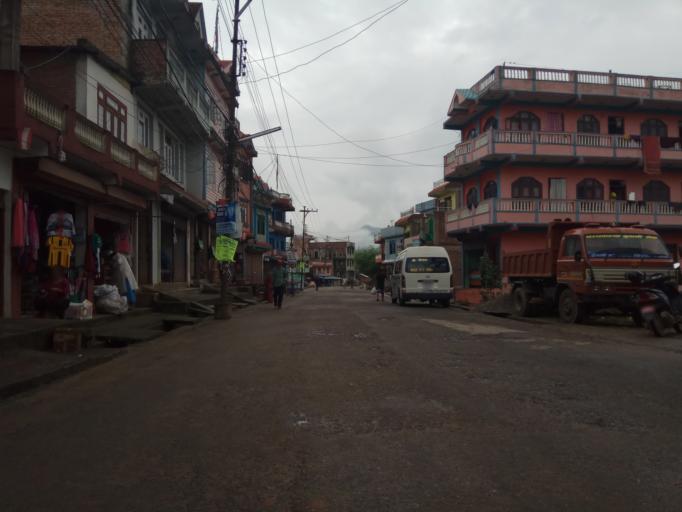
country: NP
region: Central Region
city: Kirtipur
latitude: 27.9088
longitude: 84.9006
